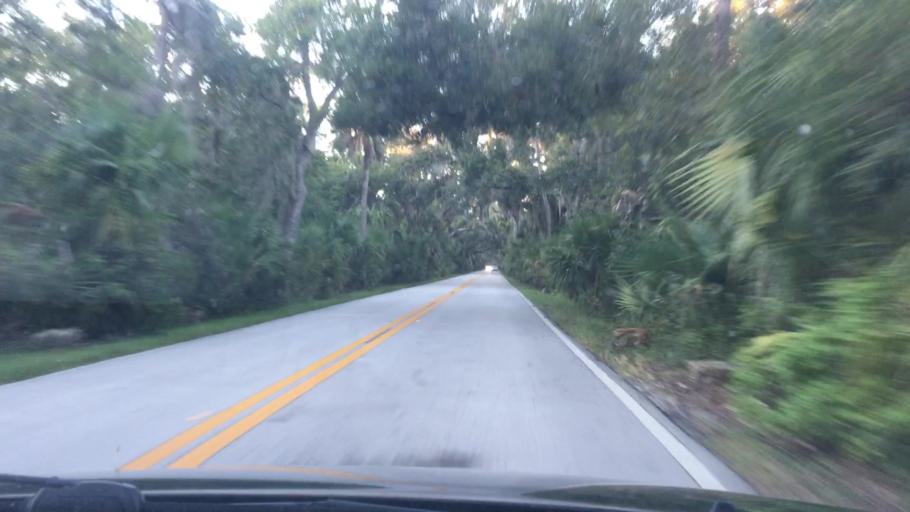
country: US
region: Florida
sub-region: Volusia County
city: Ormond-by-the-Sea
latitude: 29.3344
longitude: -81.0806
